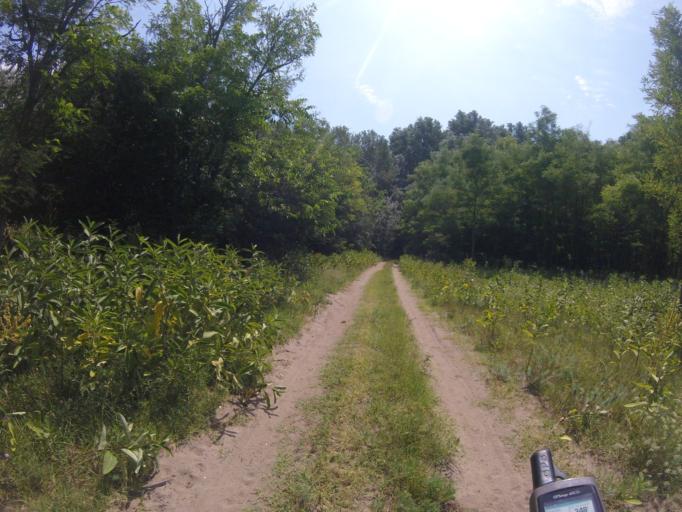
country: HU
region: Bacs-Kiskun
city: Jaszszentlaszlo
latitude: 46.6024
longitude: 19.7134
